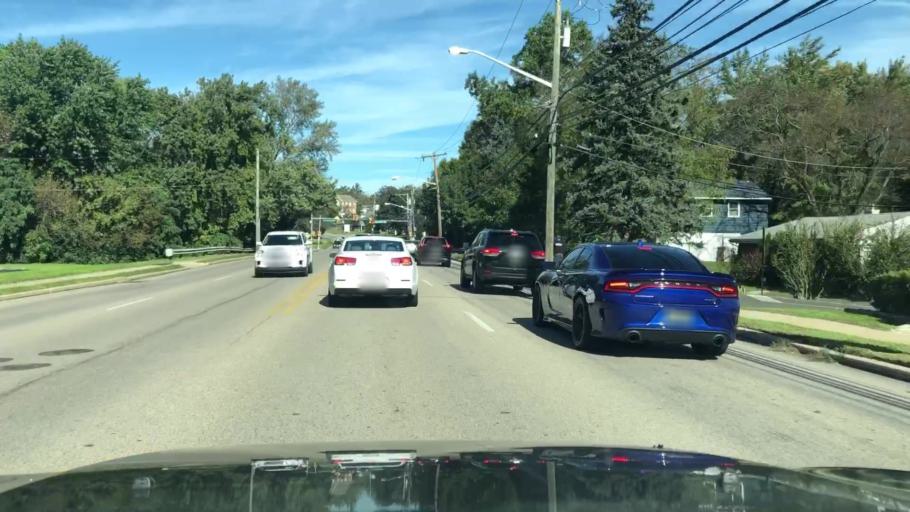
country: US
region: Pennsylvania
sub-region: Montgomery County
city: Plymouth Meeting
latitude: 40.1308
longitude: -75.3009
